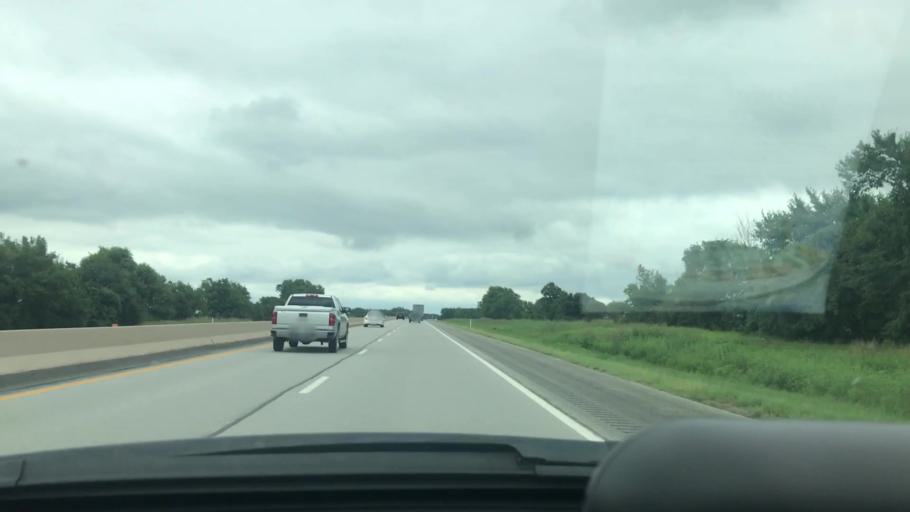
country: US
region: Oklahoma
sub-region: Ottawa County
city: Commerce
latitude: 36.9134
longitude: -94.7795
